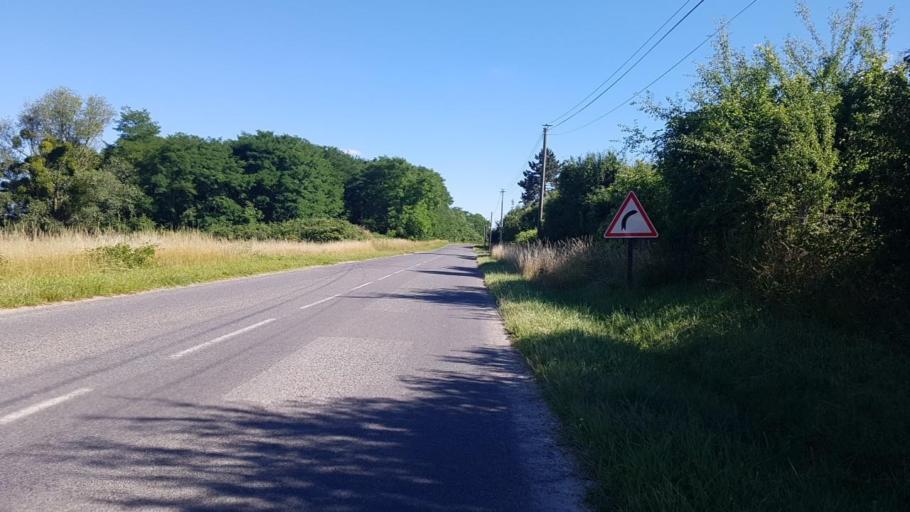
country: FR
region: Ile-de-France
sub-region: Departement de Seine-et-Marne
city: Esbly
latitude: 48.9393
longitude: 2.7993
